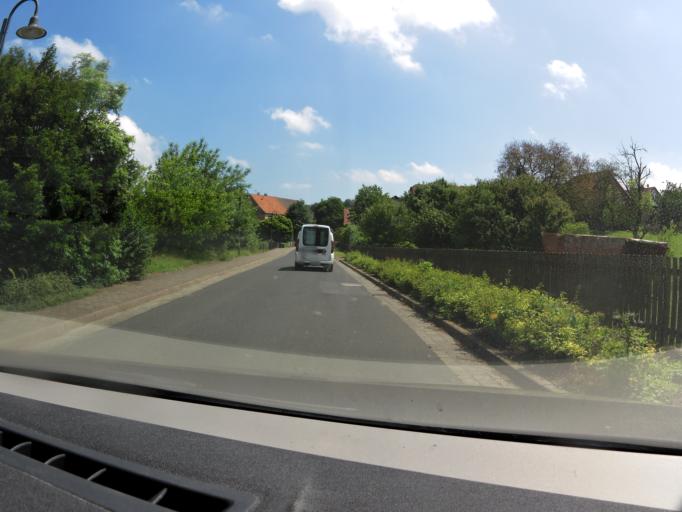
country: DE
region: Hesse
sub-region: Regierungsbezirk Kassel
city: Ronshausen
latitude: 50.9800
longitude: 9.8687
